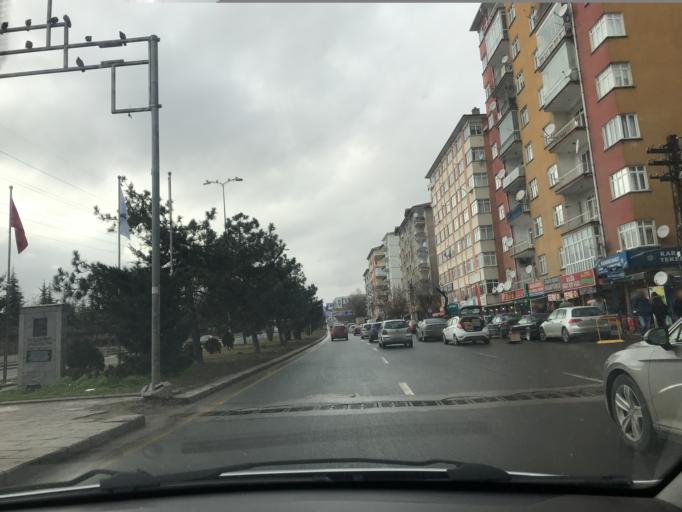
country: TR
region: Ankara
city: Batikent
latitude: 39.9583
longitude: 32.7898
